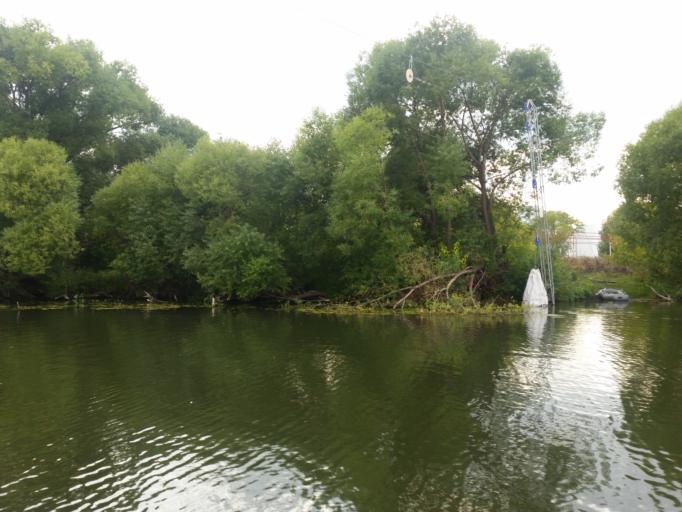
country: RU
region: Ulyanovsk
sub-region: Ulyanovskiy Rayon
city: Ulyanovsk
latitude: 54.3089
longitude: 48.3647
